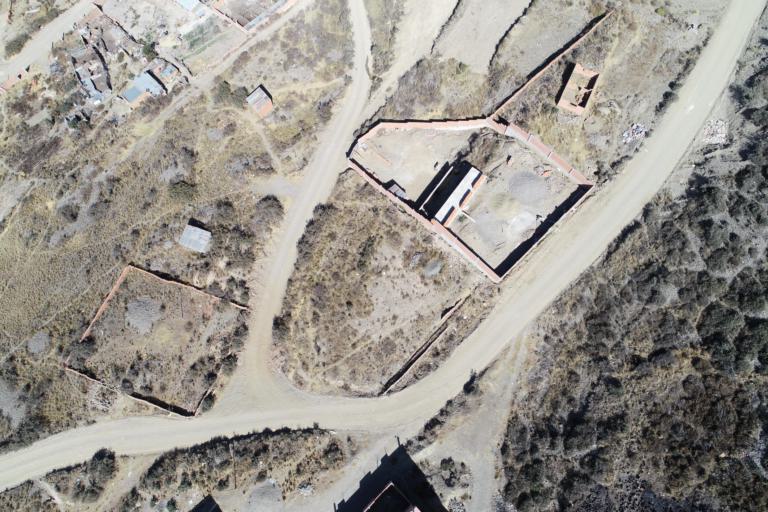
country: BO
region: La Paz
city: La Paz
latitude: -16.5422
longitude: -68.1526
